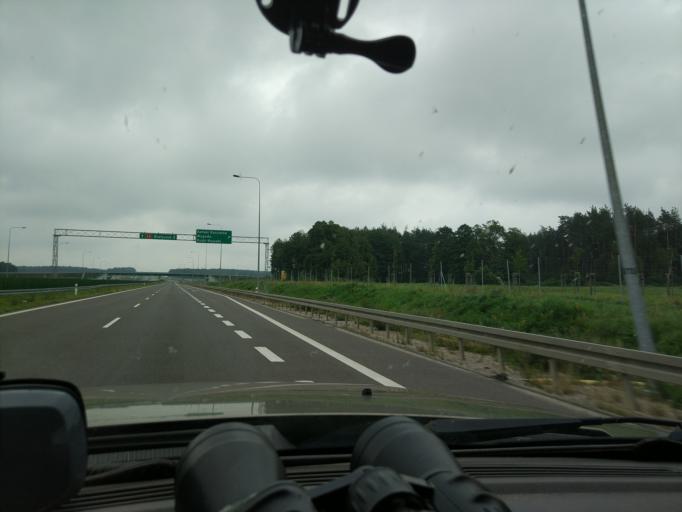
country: PL
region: Podlasie
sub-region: Powiat zambrowski
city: Rutki-Kossaki
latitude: 53.0344
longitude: 22.3467
